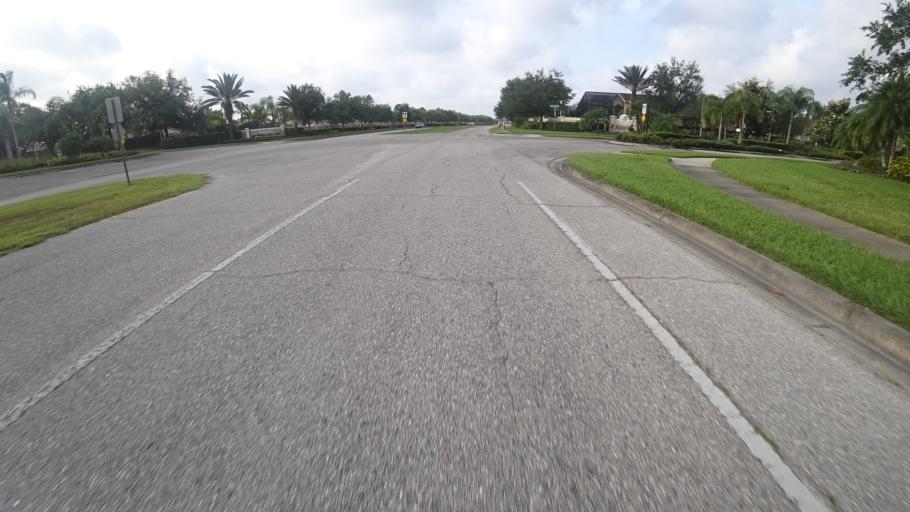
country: US
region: Florida
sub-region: Sarasota County
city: North Sarasota
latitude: 27.4234
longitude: -82.5127
